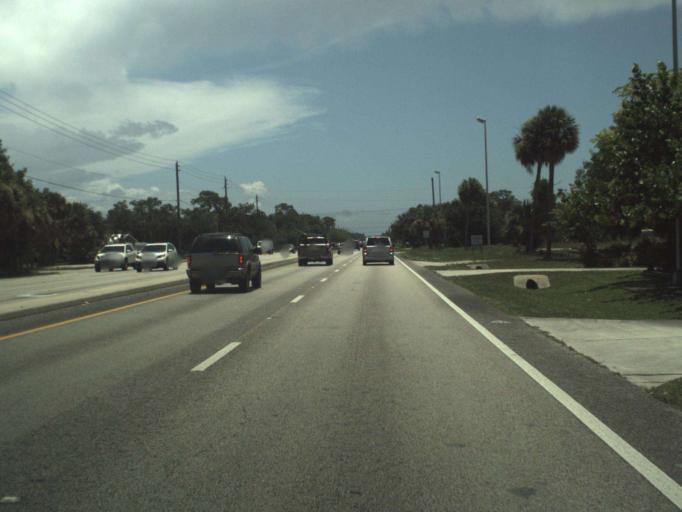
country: US
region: Florida
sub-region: Indian River County
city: Sebastian
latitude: 27.7875
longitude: -80.4550
